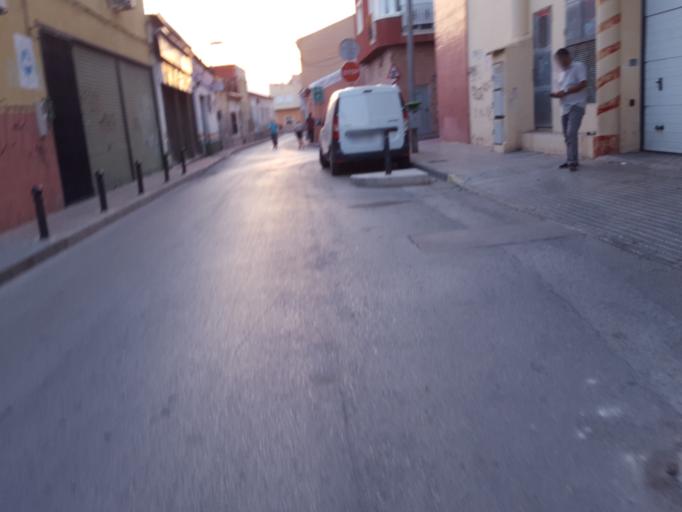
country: ES
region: Murcia
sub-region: Murcia
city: Murcia
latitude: 37.9755
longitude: -1.1371
